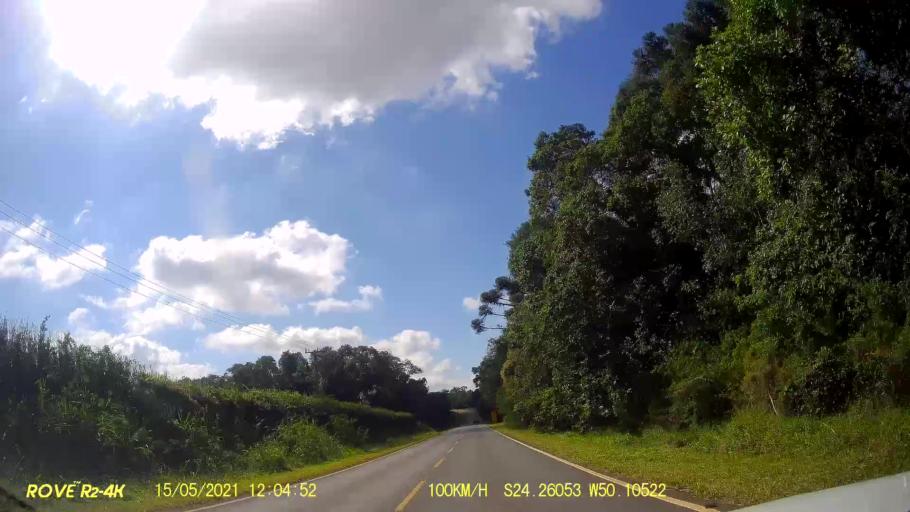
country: BR
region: Parana
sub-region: Pirai Do Sul
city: Pirai do Sul
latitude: -24.2605
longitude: -50.1052
